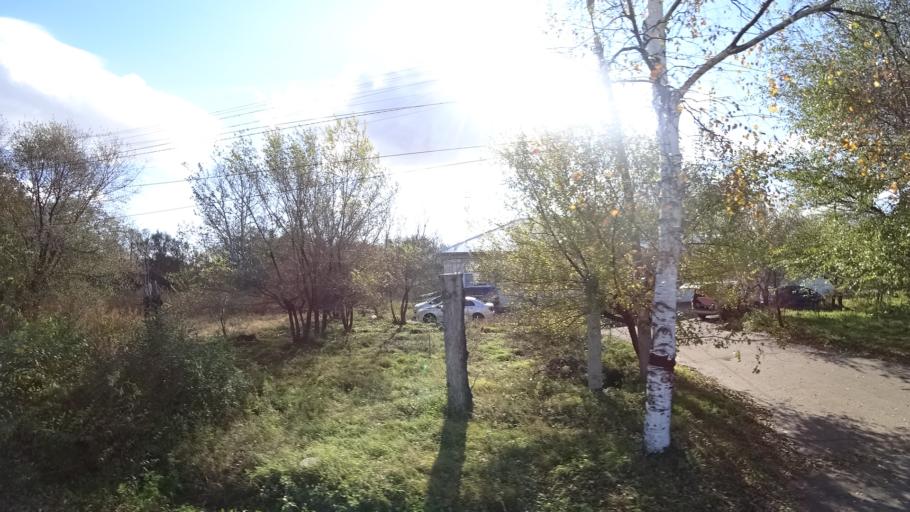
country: RU
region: Khabarovsk Krai
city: Amursk
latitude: 50.0981
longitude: 136.4966
